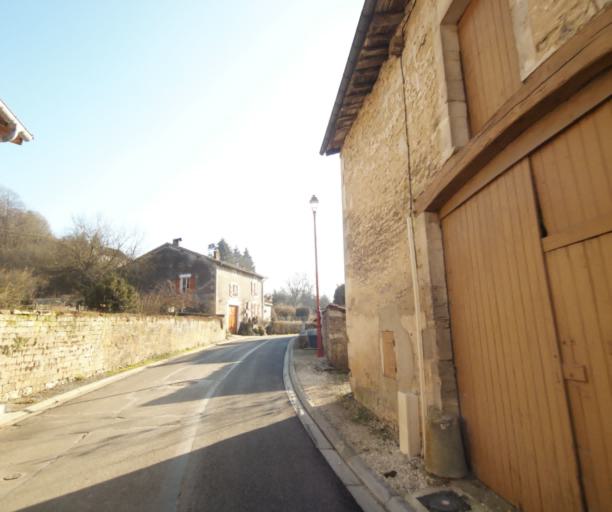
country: FR
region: Champagne-Ardenne
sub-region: Departement de la Haute-Marne
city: Chevillon
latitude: 48.4982
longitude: 5.1927
